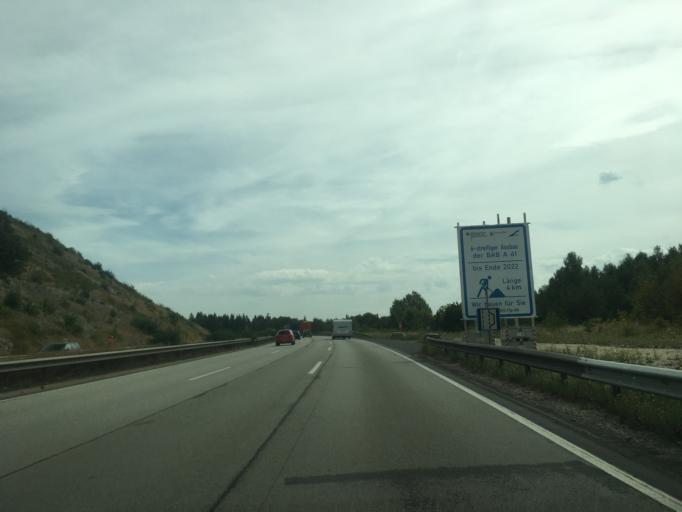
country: DE
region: Rheinland-Pfalz
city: Dichtelbach
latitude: 49.9841
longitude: 7.7049
